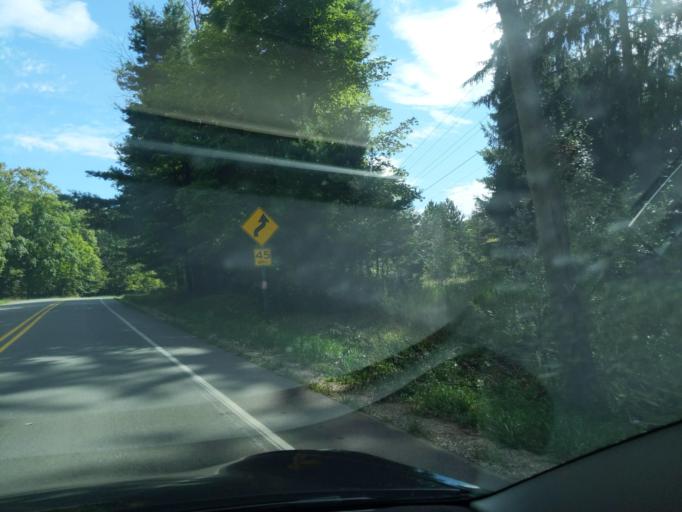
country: US
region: Michigan
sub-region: Antrim County
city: Bellaire
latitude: 45.0460
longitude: -85.3049
